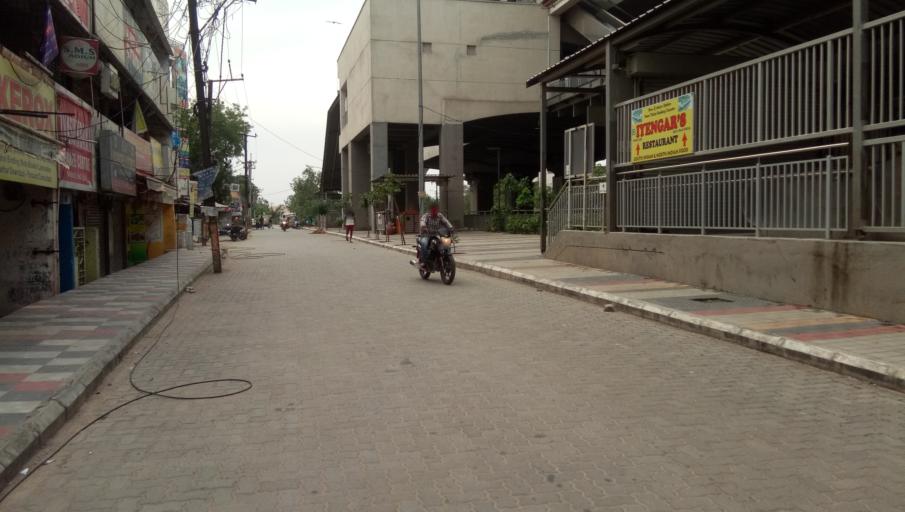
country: IN
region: Telangana
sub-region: Rangareddi
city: Lal Bahadur Nagar
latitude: 17.3494
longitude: 78.5479
